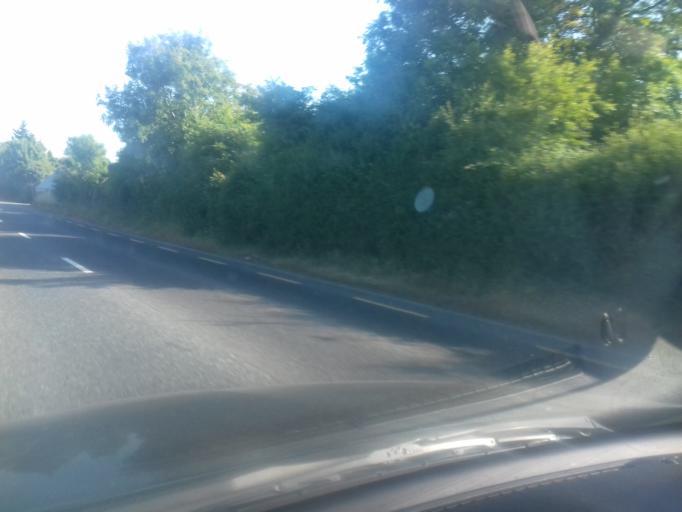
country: IE
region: Leinster
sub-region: Fingal County
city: Blanchardstown
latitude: 53.4538
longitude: -6.3469
